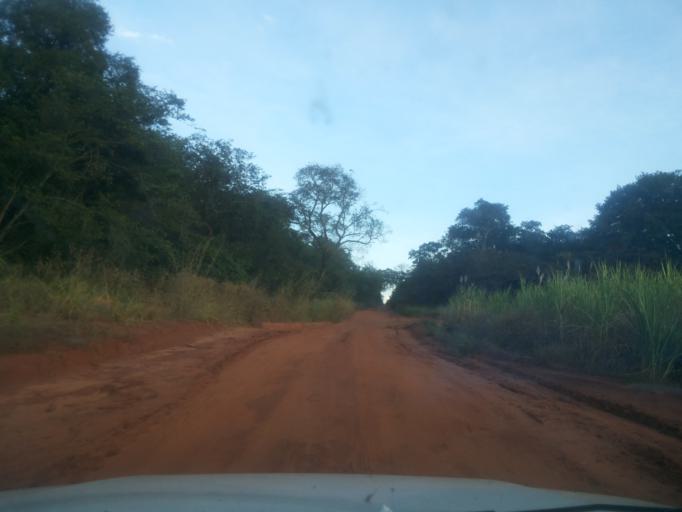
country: BR
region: Minas Gerais
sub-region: Santa Vitoria
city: Santa Vitoria
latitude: -19.0048
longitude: -50.3730
